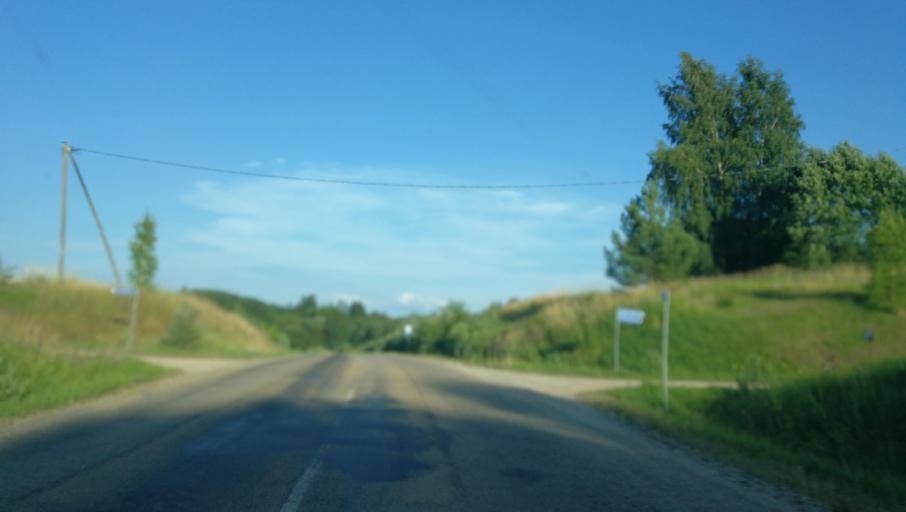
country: LV
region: Priekuli
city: Priekuli
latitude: 57.2604
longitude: 25.3599
